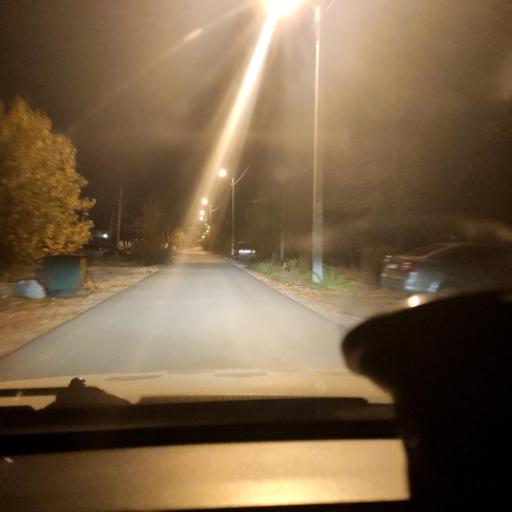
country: RU
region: Perm
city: Perm
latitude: 57.9782
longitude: 56.3098
